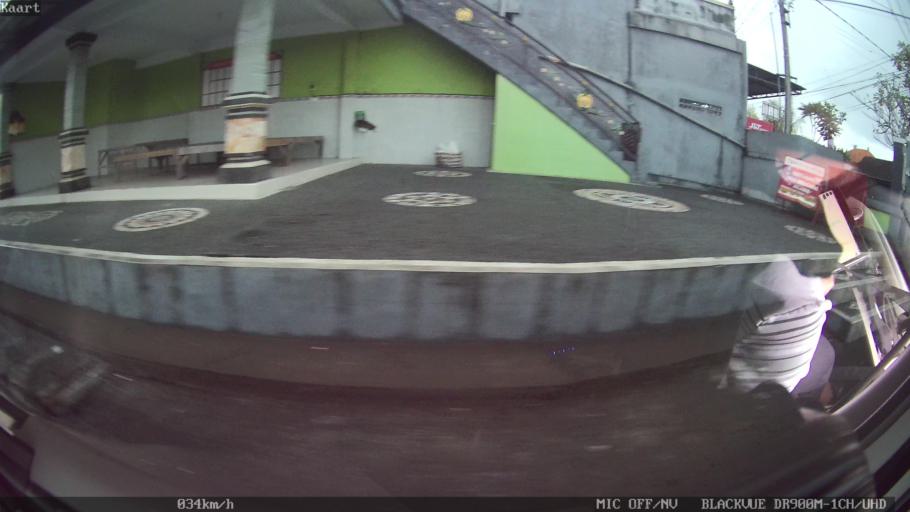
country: ID
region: Bali
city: Banjar Sempidi
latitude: -8.5234
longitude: 115.1959
